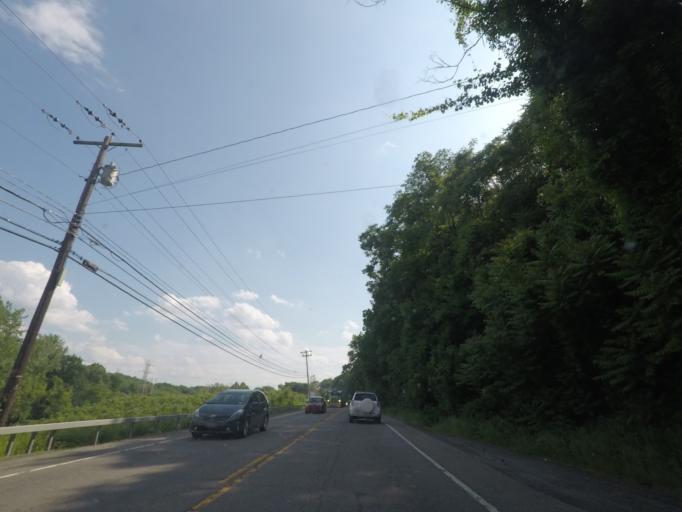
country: US
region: New York
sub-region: Ulster County
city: Marlboro
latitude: 41.5911
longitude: -73.9802
